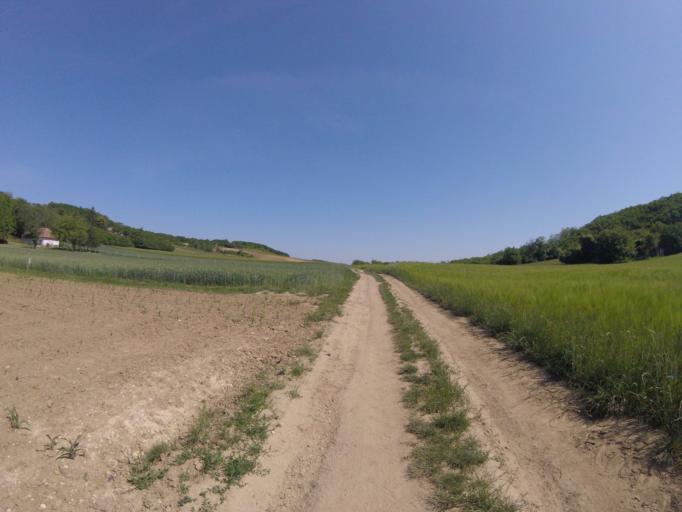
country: HU
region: Zala
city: Zalaszentgrot
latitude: 46.9104
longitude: 17.0553
